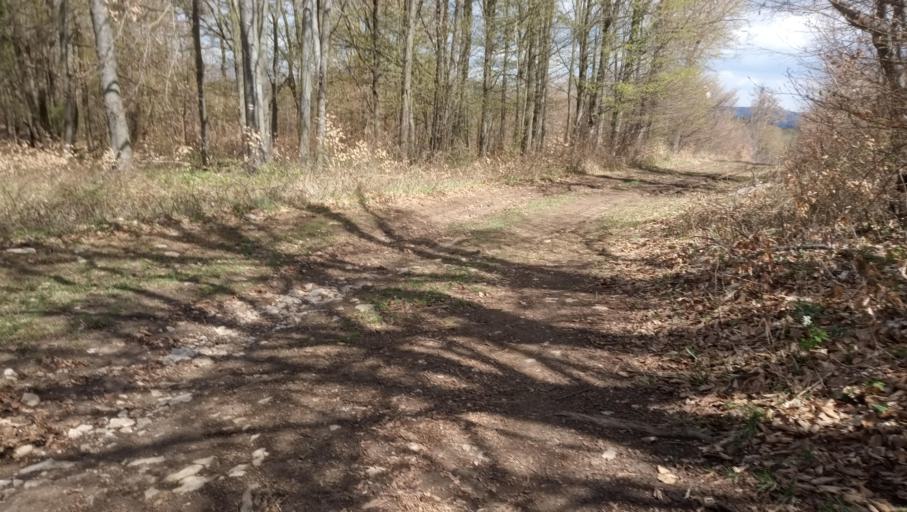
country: HU
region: Veszprem
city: Herend
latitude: 47.2023
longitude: 17.7559
